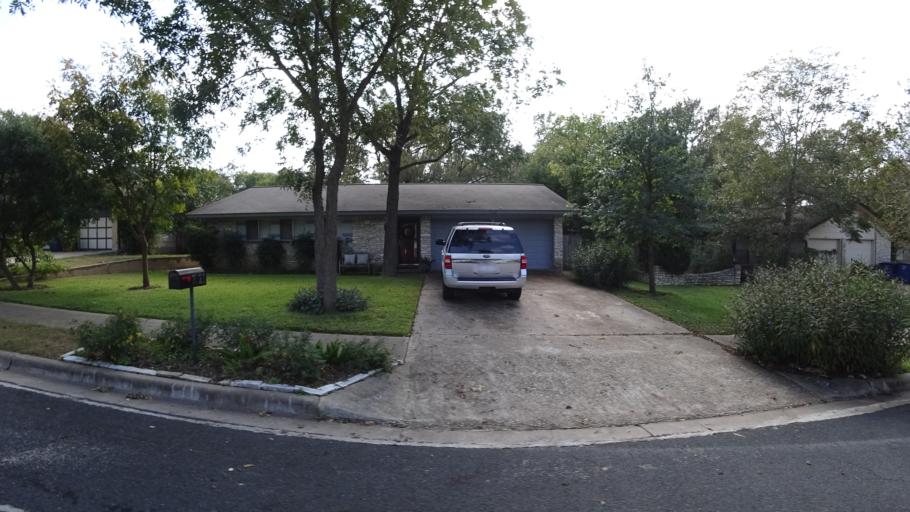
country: US
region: Texas
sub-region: Travis County
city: Shady Hollow
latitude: 30.2019
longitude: -97.8160
